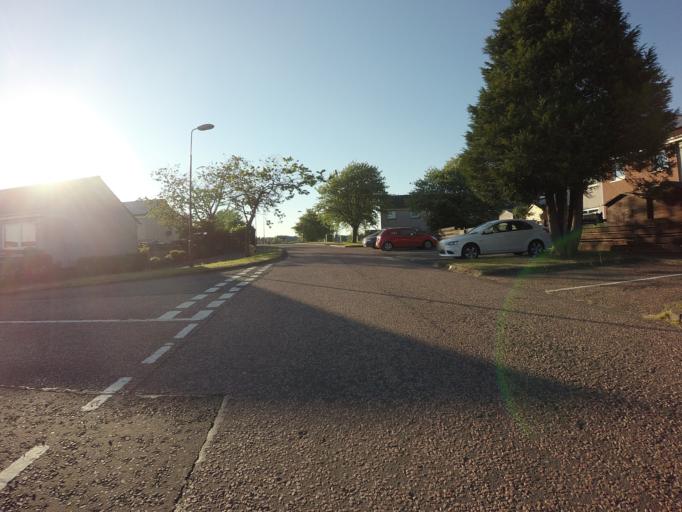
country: GB
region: Scotland
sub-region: West Lothian
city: Livingston
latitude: 55.8997
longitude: -3.5567
